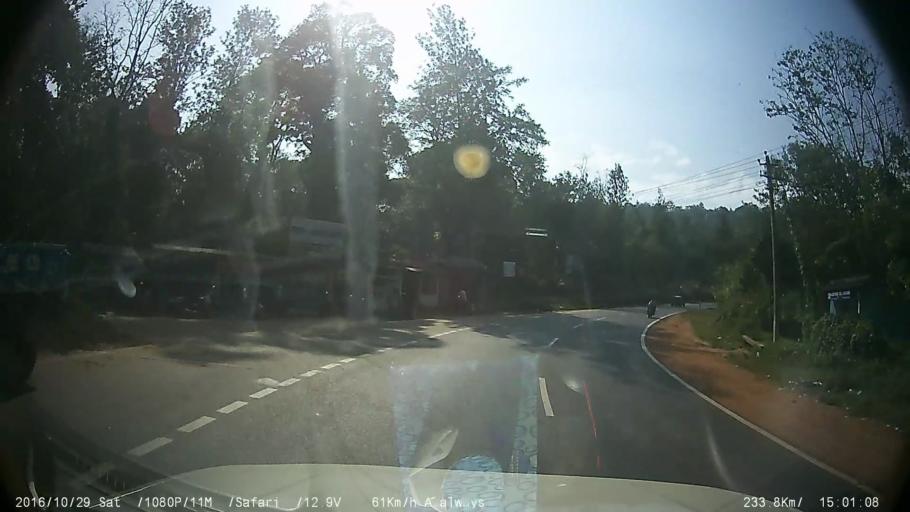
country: IN
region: Karnataka
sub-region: Kodagu
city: Suntikoppa
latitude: 12.4410
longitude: 75.8512
